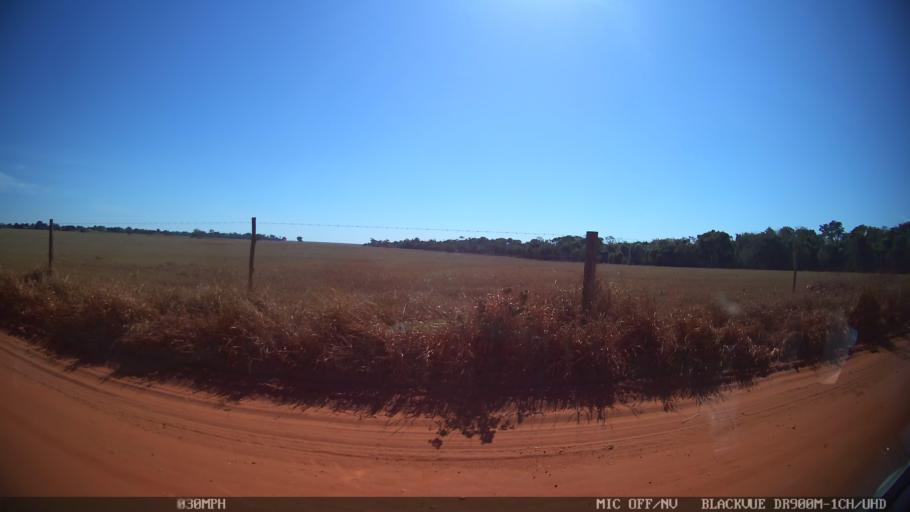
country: BR
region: Sao Paulo
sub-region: Sao Jose Do Rio Preto
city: Sao Jose do Rio Preto
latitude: -20.7414
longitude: -49.4235
